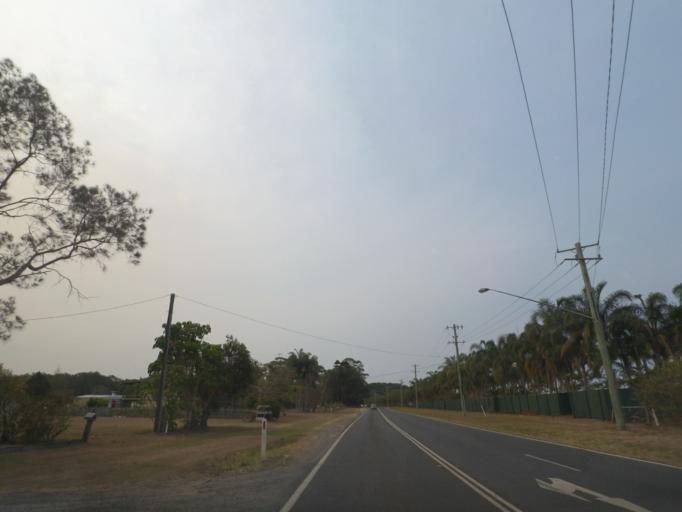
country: AU
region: New South Wales
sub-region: Tweed
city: Kingscliff
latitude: -28.2570
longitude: 153.5597
